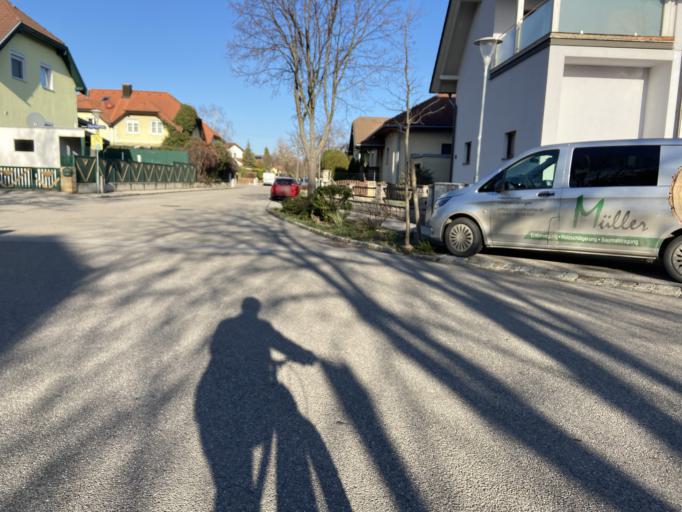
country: AT
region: Lower Austria
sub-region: Politischer Bezirk Modling
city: Neu-Guntramsdorf
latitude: 48.0566
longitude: 16.3124
